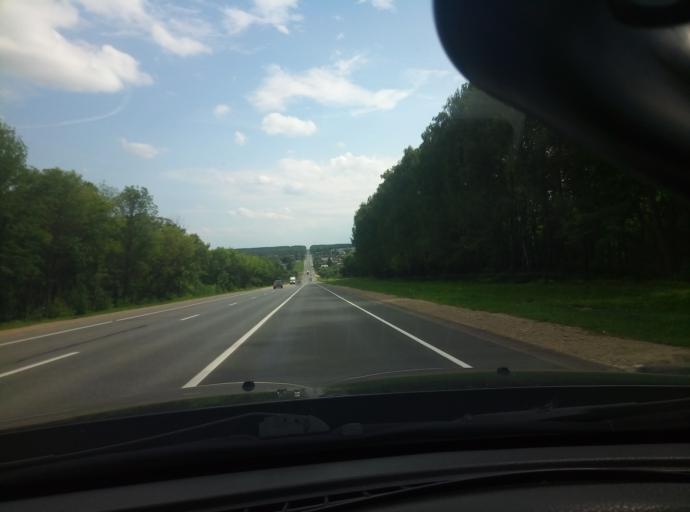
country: RU
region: Tula
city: Gorelki
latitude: 54.3100
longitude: 37.5678
